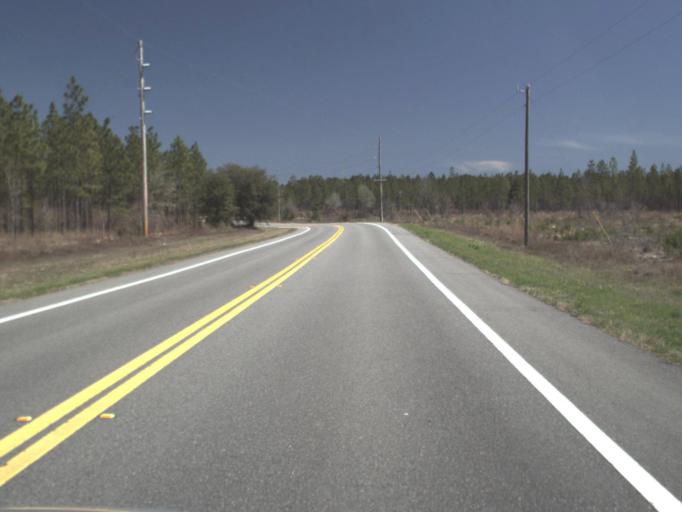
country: US
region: Florida
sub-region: Gadsden County
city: Quincy
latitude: 30.4171
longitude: -84.6538
